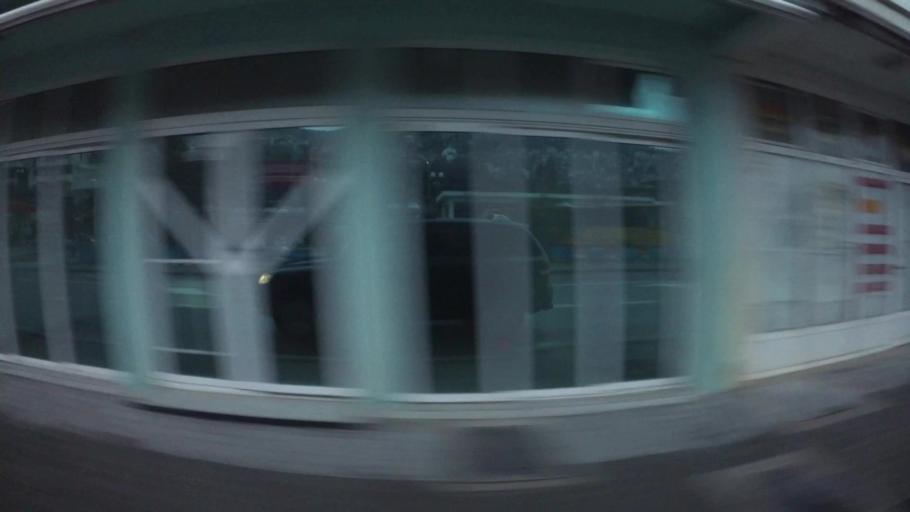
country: BA
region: Federation of Bosnia and Herzegovina
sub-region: Hercegovacko-Bosanski Kanton
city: Mostar
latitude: 43.3477
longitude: 17.8130
